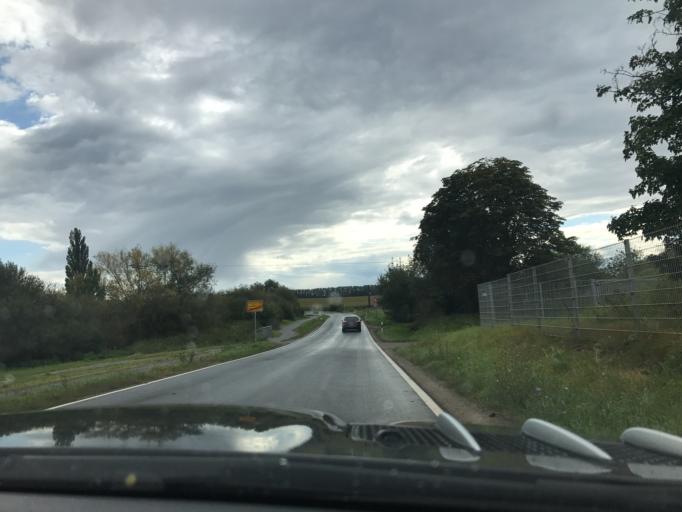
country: DE
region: Thuringia
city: Niederdorla
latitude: 51.1531
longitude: 10.4407
